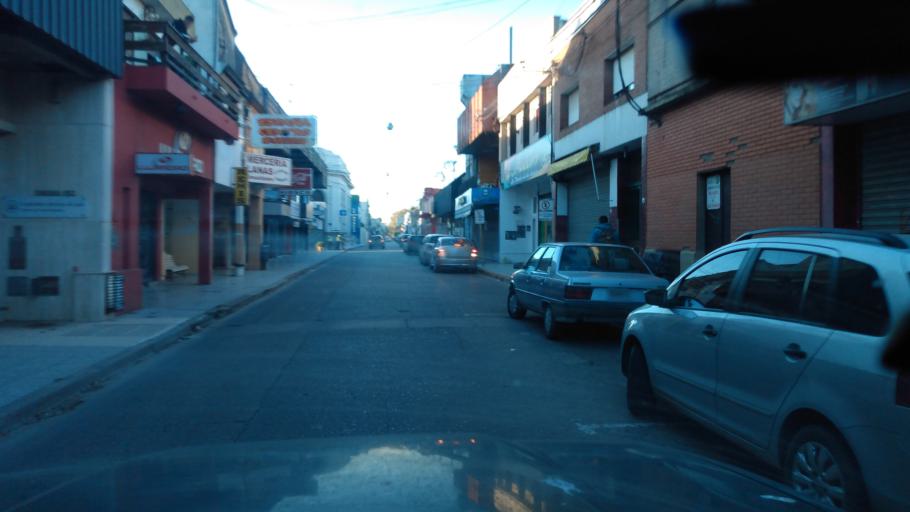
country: AR
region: Buenos Aires
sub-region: Partido de Lujan
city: Lujan
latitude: -34.5655
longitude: -59.1182
